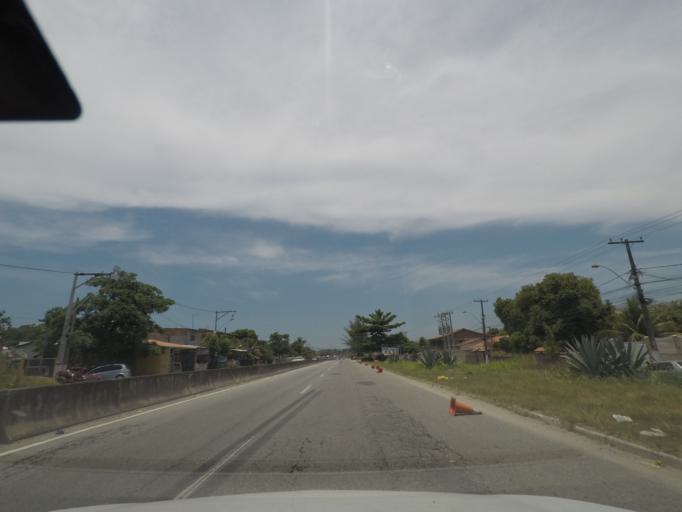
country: BR
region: Rio de Janeiro
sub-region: Marica
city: Marica
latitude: -22.9249
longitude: -42.8637
